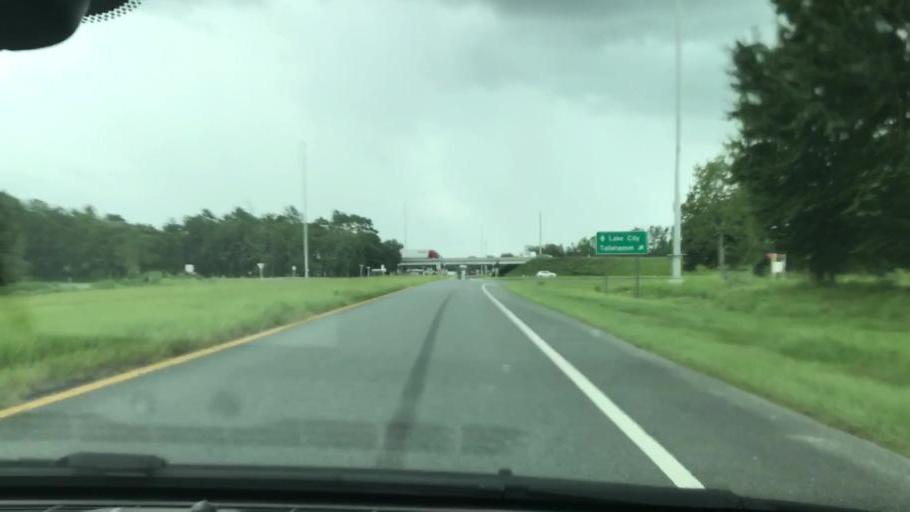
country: US
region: Florida
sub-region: Madison County
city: Madison
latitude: 30.3823
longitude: -83.2990
